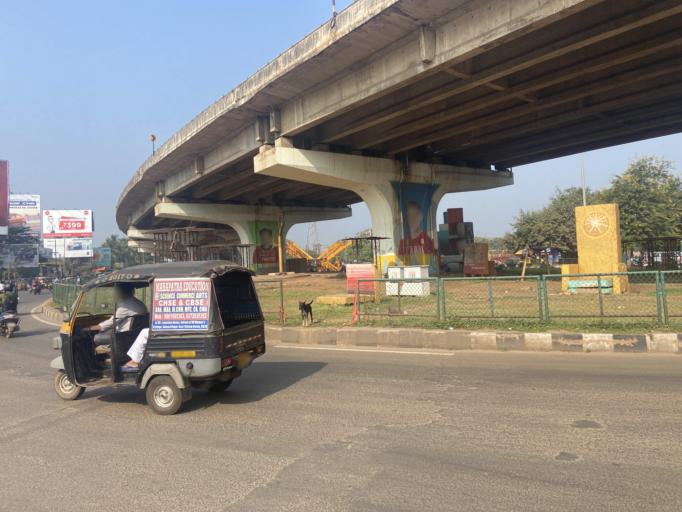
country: IN
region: Odisha
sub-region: Khordha
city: Bhubaneshwar
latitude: 20.2952
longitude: 85.8579
